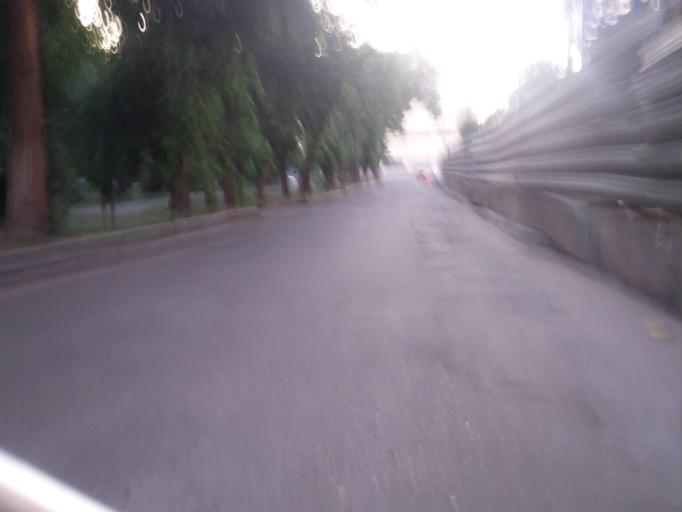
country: RU
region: Voronezj
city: Voronezh
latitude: 51.6536
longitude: 39.1776
